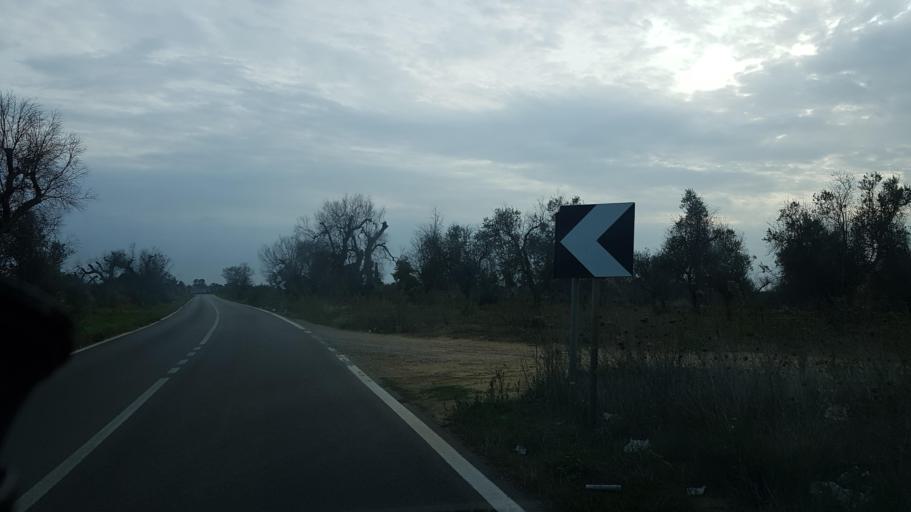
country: IT
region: Apulia
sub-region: Provincia di Lecce
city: Trepuzzi
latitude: 40.4212
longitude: 18.0732
